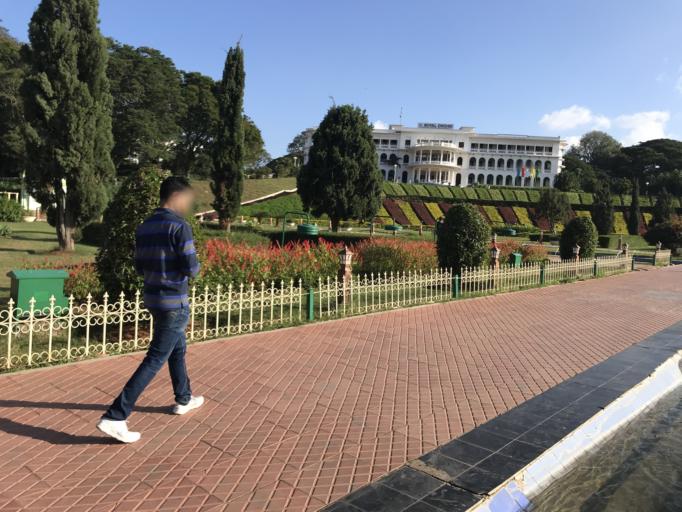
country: IN
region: Karnataka
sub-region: Mandya
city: Shrirangapattana
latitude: 12.4209
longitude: 76.5728
